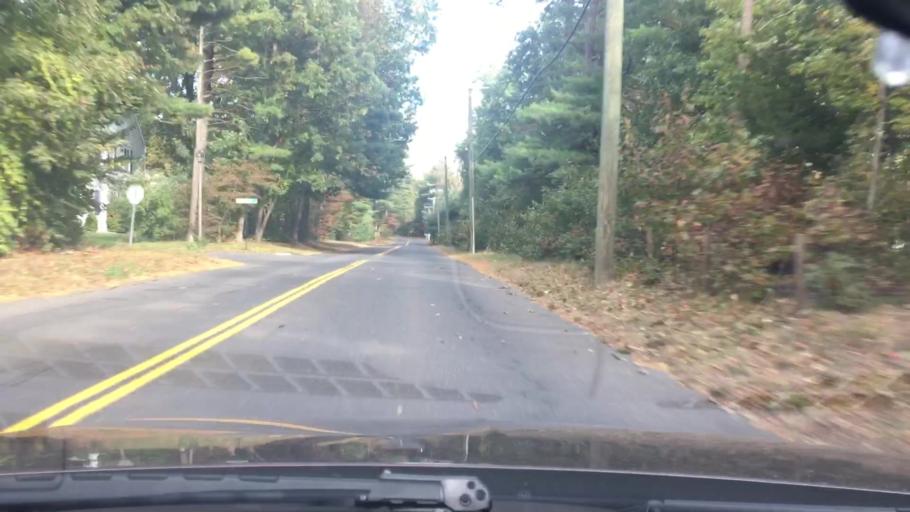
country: US
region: Connecticut
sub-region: Hartford County
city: Plainville
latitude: 41.7006
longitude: -72.8593
